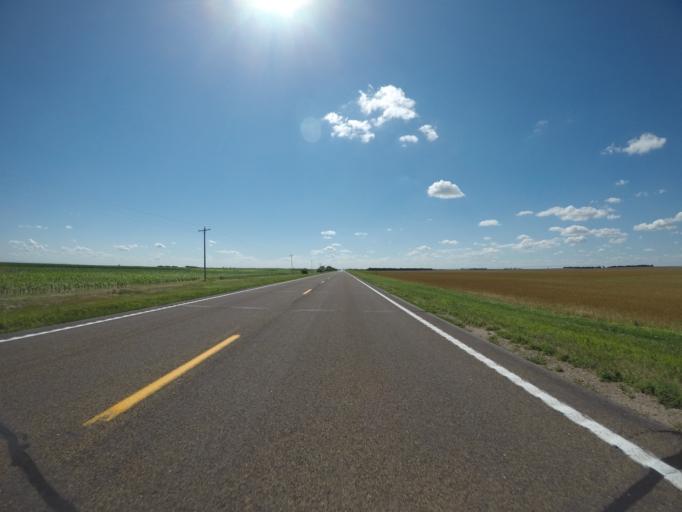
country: US
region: Nebraska
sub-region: Chase County
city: Imperial
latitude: 40.5377
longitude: -101.8758
